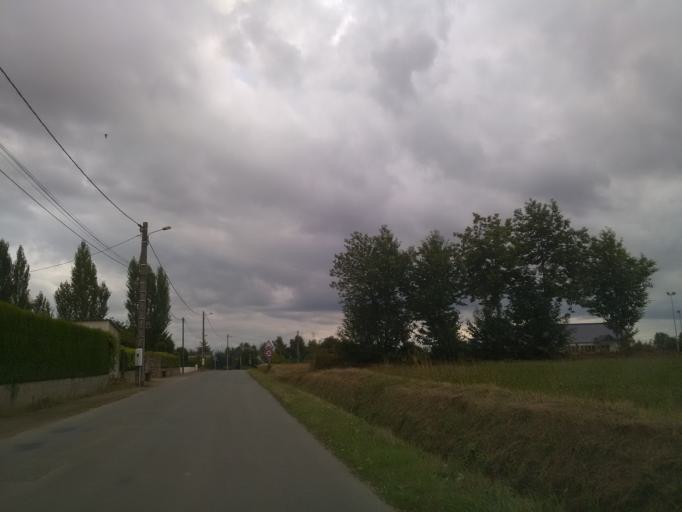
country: FR
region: Brittany
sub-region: Departement d'Ille-et-Vilaine
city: Vignoc
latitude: 48.2474
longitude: -1.7862
